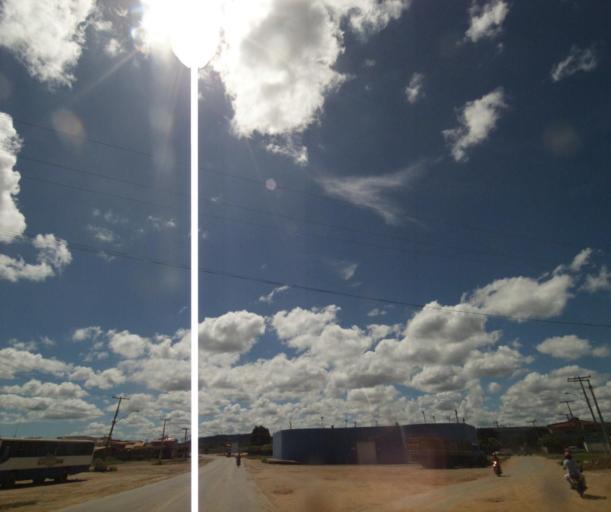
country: BR
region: Bahia
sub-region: Sao Felix Do Coribe
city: Santa Maria da Vitoria
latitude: -13.4074
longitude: -44.1885
